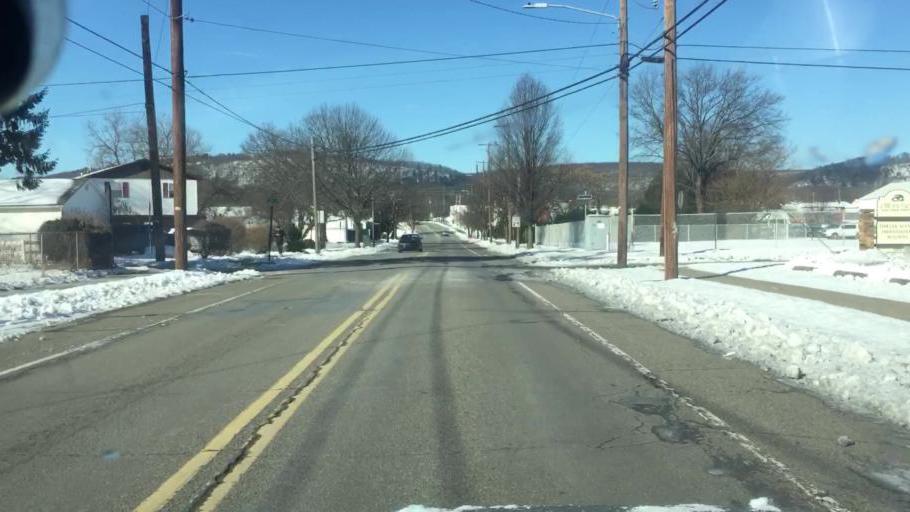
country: US
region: Pennsylvania
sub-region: Luzerne County
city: East Berwick
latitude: 41.0619
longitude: -76.2271
